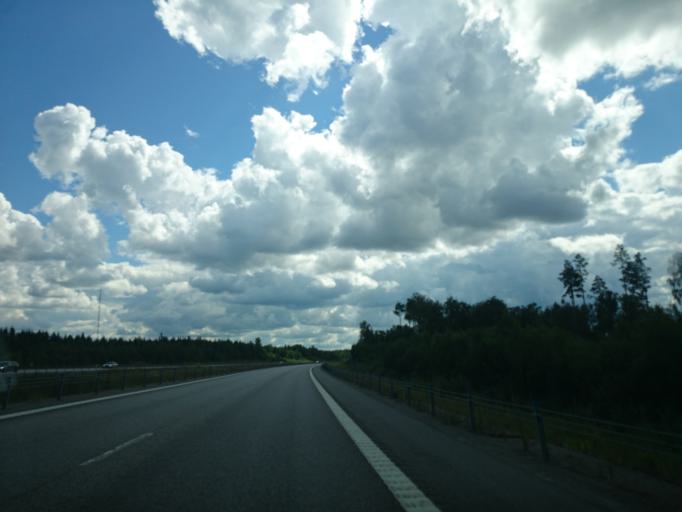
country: SE
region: Uppsala
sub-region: Tierps Kommun
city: Tierp
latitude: 60.4082
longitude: 17.4665
